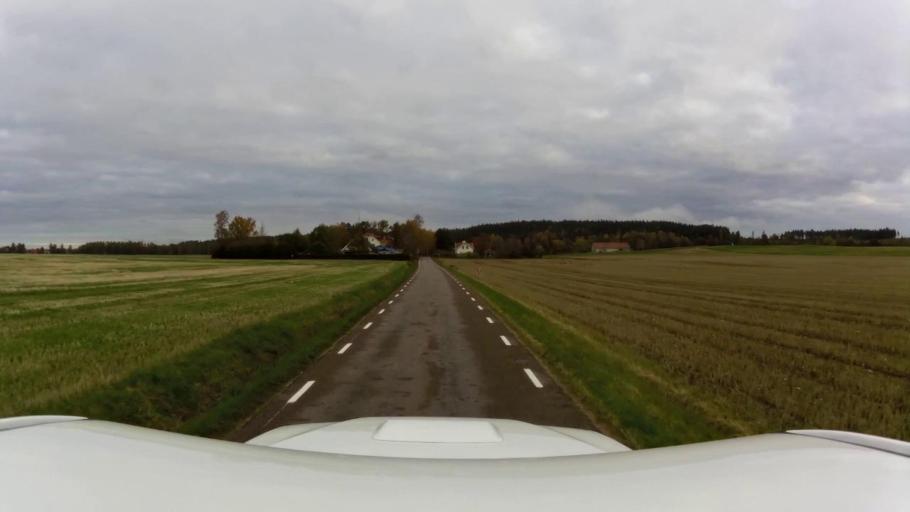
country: SE
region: OEstergoetland
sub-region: Linkopings Kommun
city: Ljungsbro
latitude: 58.5329
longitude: 15.4187
